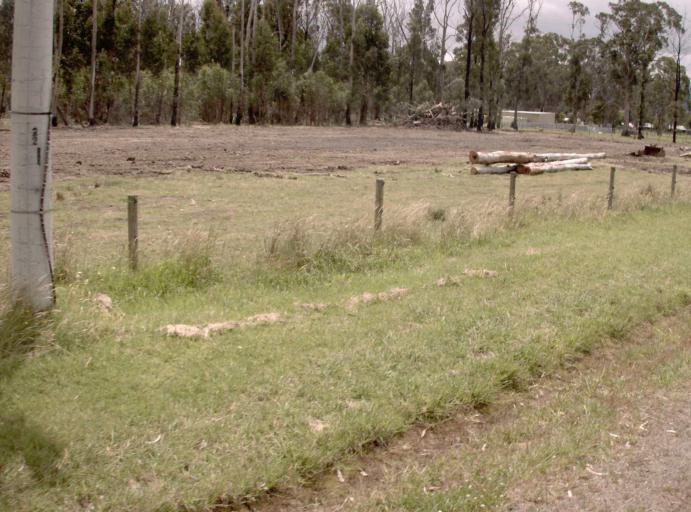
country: AU
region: Victoria
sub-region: Latrobe
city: Traralgon
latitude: -38.5324
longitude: 146.6584
